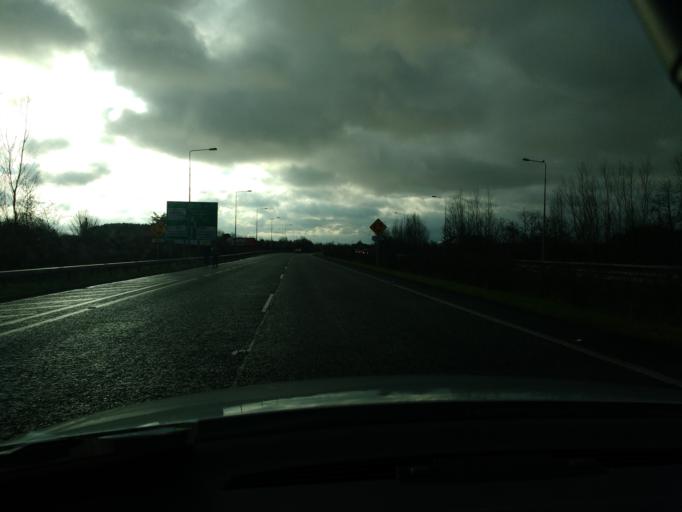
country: IE
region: Munster
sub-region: An Clar
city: Shannon
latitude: 52.7170
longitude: -8.8818
